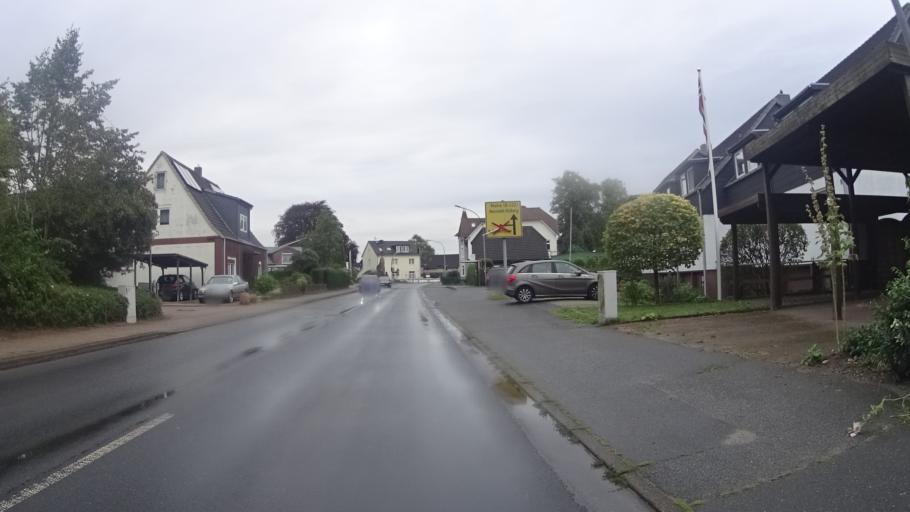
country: DE
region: Schleswig-Holstein
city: Alveslohe
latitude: 53.7868
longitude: 9.9133
